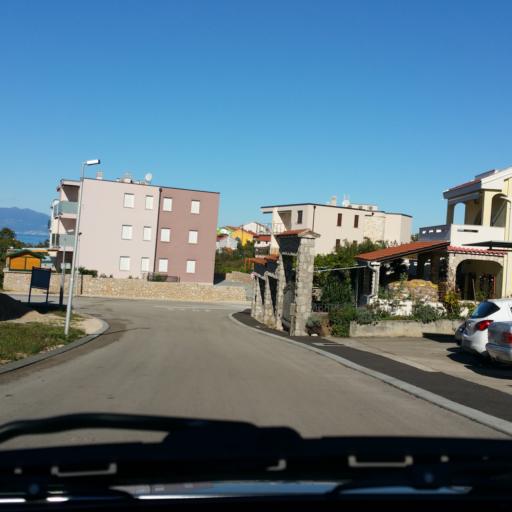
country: HR
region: Primorsko-Goranska
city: Njivice
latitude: 45.1532
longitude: 14.5412
